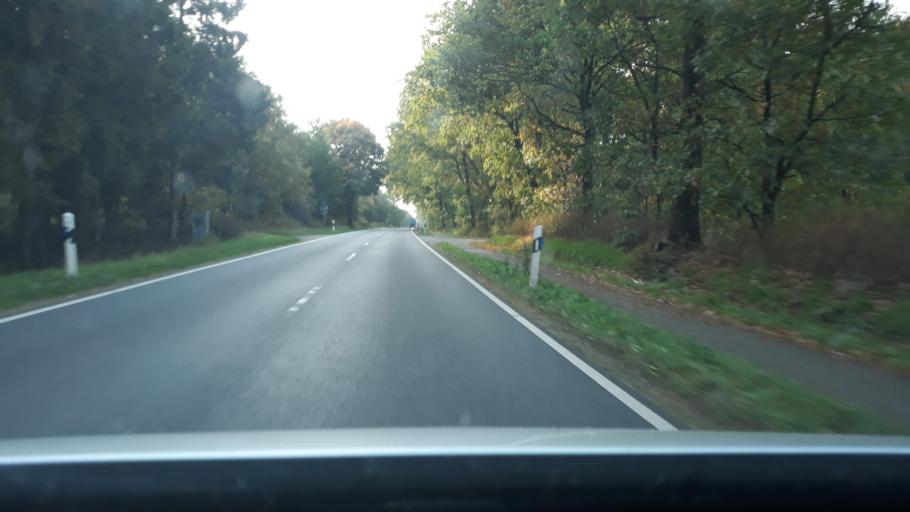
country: DE
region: Schleswig-Holstein
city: Kropp
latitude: 54.3970
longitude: 9.5505
